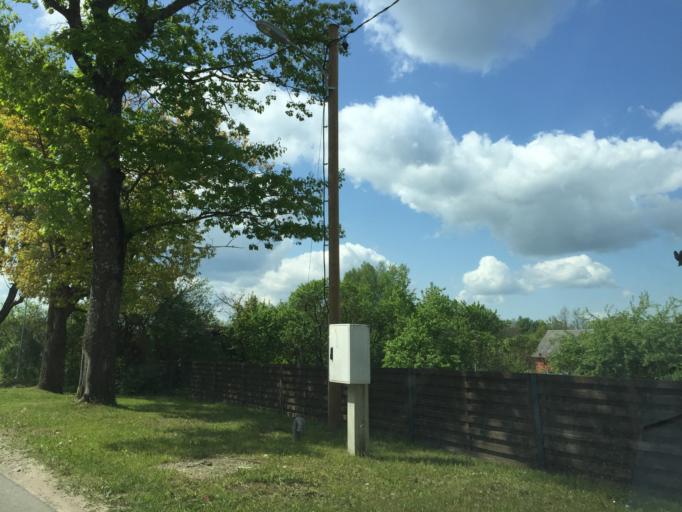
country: LV
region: Baldone
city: Baldone
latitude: 56.7391
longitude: 24.3777
